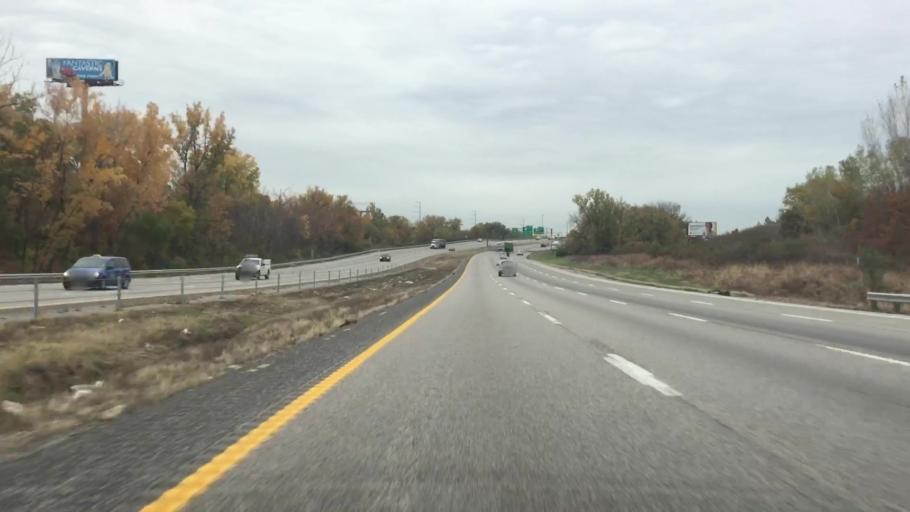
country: US
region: Missouri
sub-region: Jackson County
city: Sugar Creek
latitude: 39.0763
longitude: -94.4897
